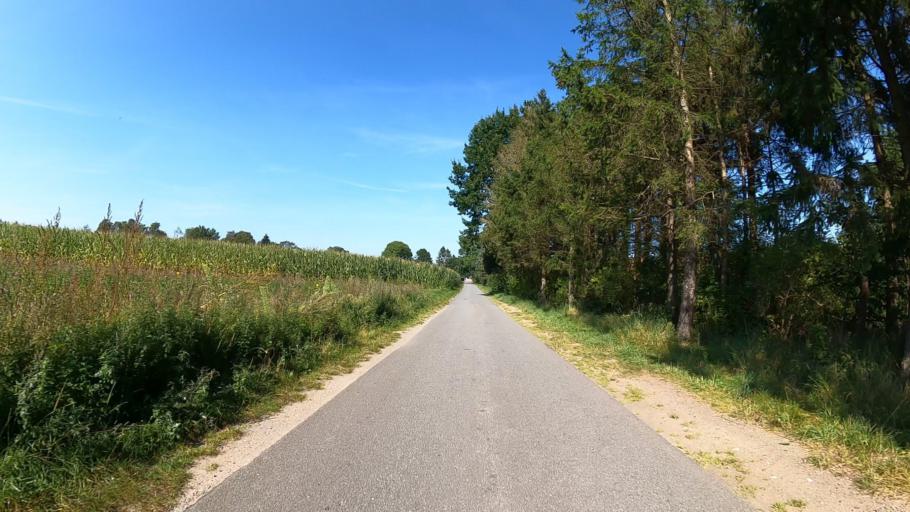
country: DE
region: Schleswig-Holstein
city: Nutzen
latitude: 53.8595
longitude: 9.9206
